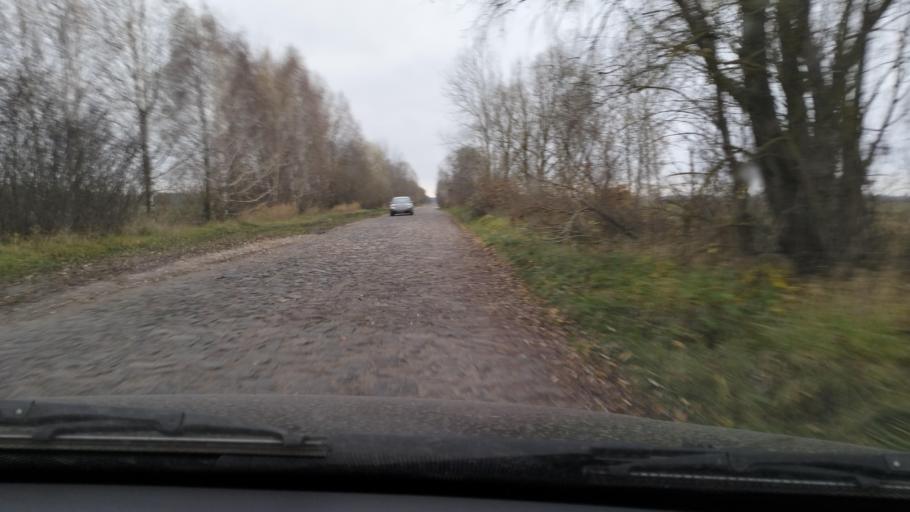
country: BY
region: Brest
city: Davyd-Haradok
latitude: 51.9923
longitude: 27.2054
